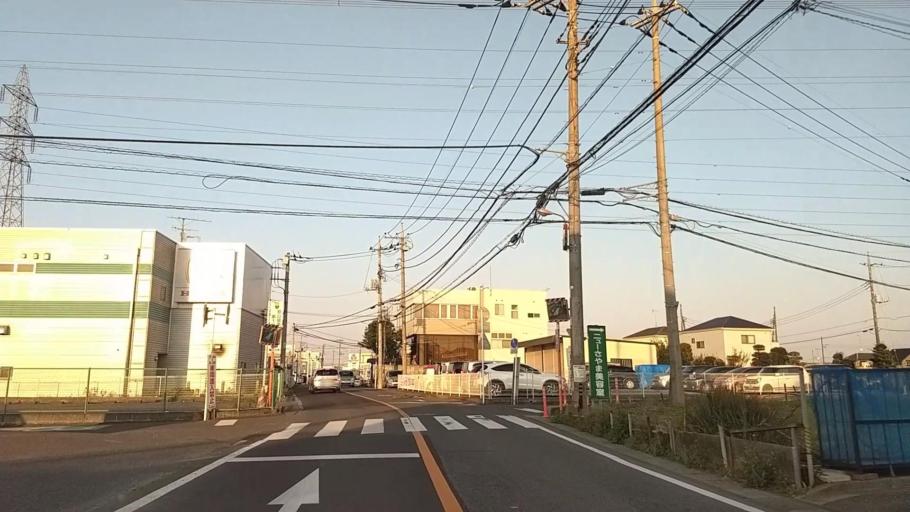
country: JP
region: Saitama
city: Sayama
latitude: 35.8704
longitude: 139.4237
